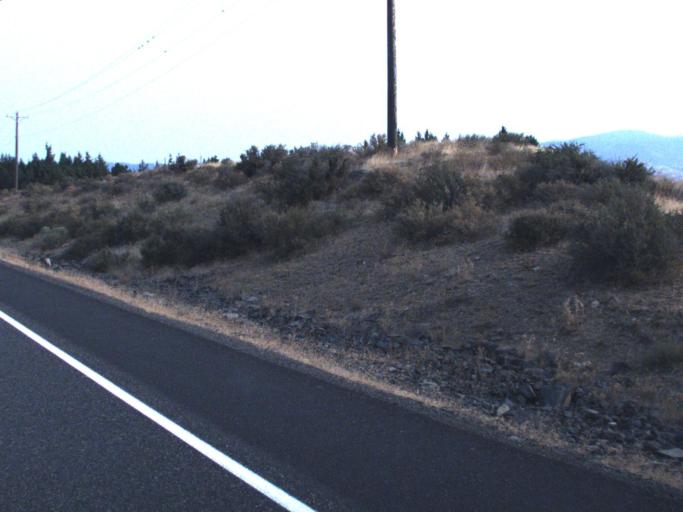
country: US
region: Washington
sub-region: Kittitas County
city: Ellensburg
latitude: 47.1085
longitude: -120.6645
